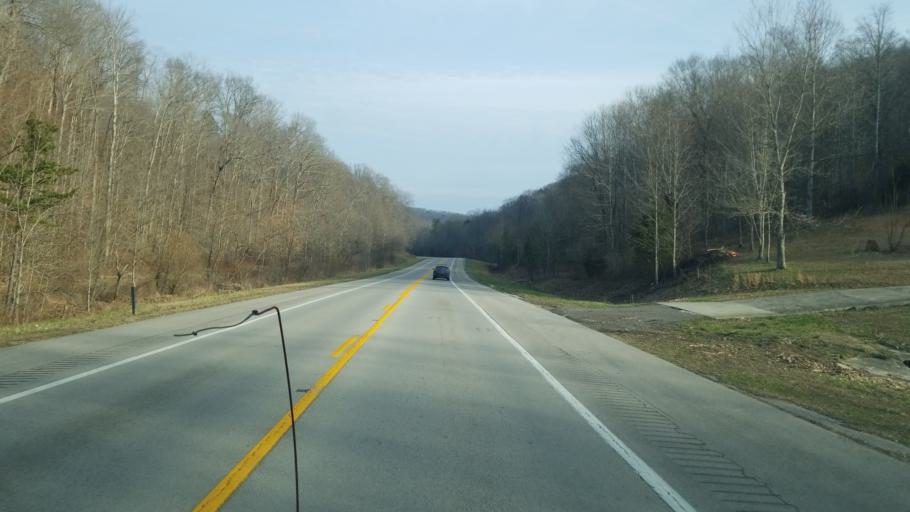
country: US
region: Kentucky
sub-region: Russell County
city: Russell Springs
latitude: 37.1511
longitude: -85.0248
